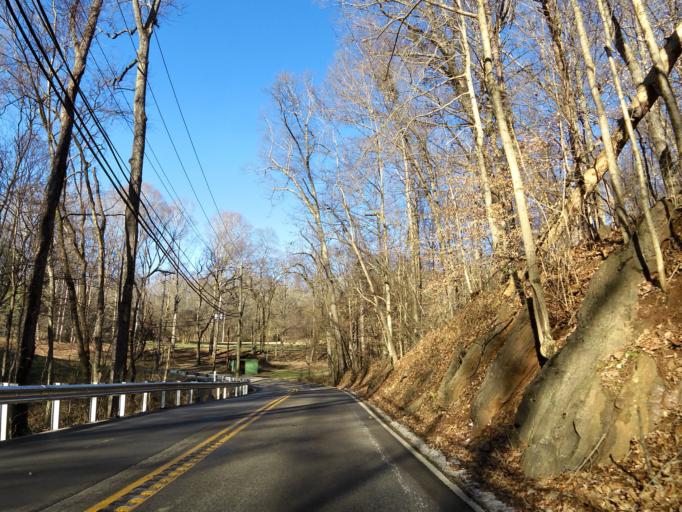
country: US
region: Tennessee
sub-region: Knox County
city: Knoxville
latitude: 35.9071
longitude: -83.9838
